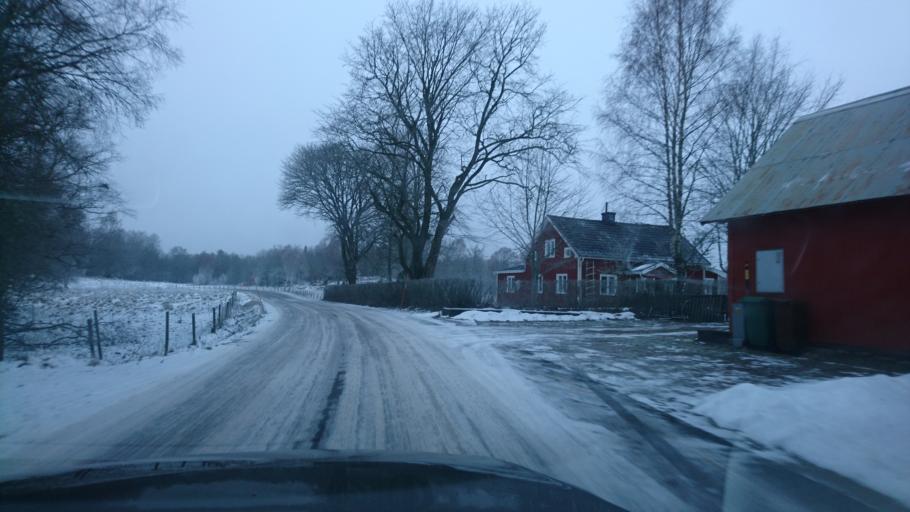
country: SE
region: Vaestra Goetaland
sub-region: Falkopings Kommun
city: Floby
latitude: 58.0742
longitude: 13.3938
